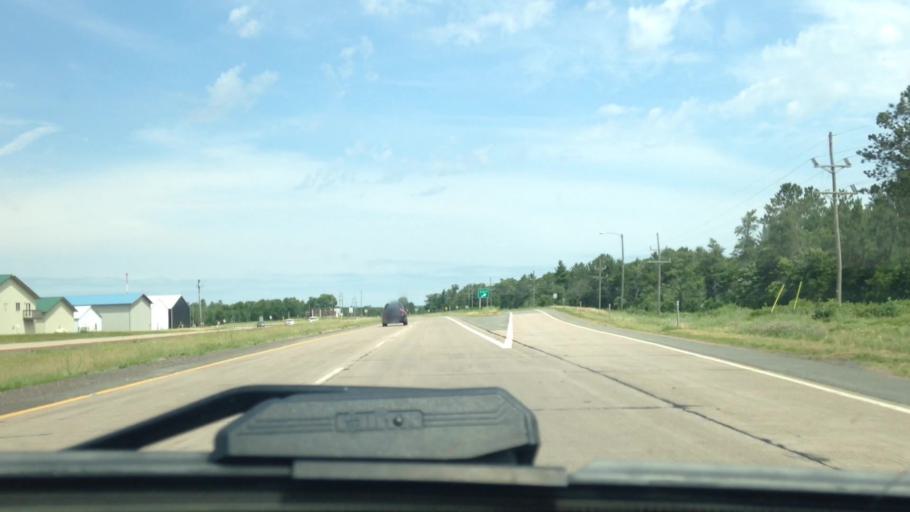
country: US
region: Wisconsin
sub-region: Douglas County
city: Lake Nebagamon
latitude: 46.3165
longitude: -91.8119
